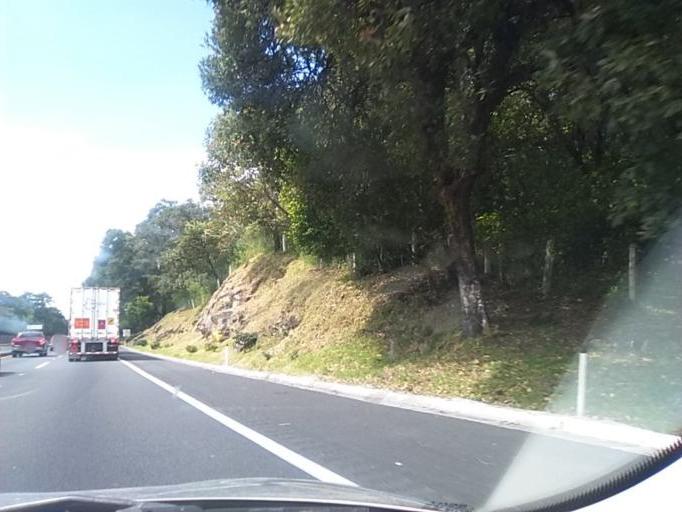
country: MX
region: Morelos
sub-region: Cuernavaca
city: Villa Santiago
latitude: 19.0052
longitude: -99.1844
